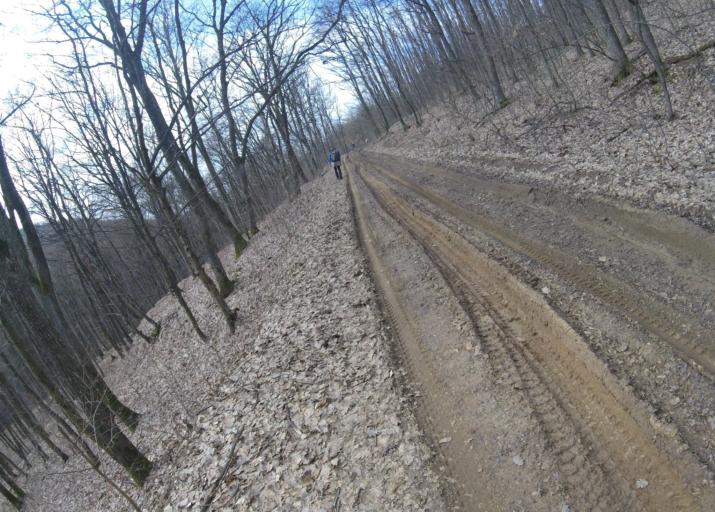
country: HU
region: Heves
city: Belapatfalva
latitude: 48.0177
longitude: 20.3522
